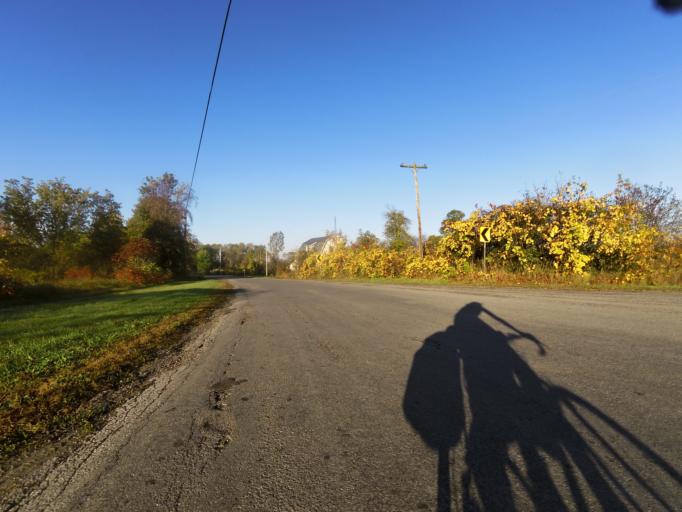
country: CA
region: Ontario
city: Belleville
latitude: 44.0244
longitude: -77.4871
